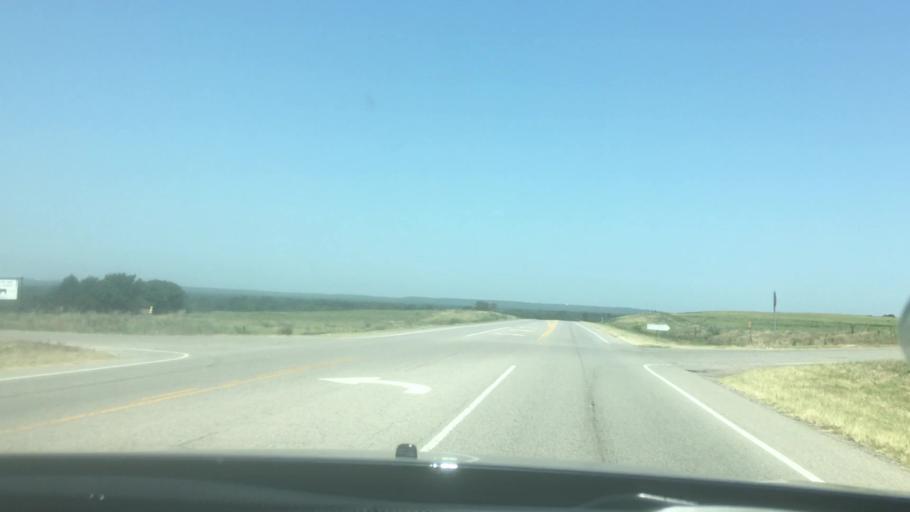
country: US
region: Oklahoma
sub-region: Pontotoc County
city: Ada
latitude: 34.6802
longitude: -96.5824
